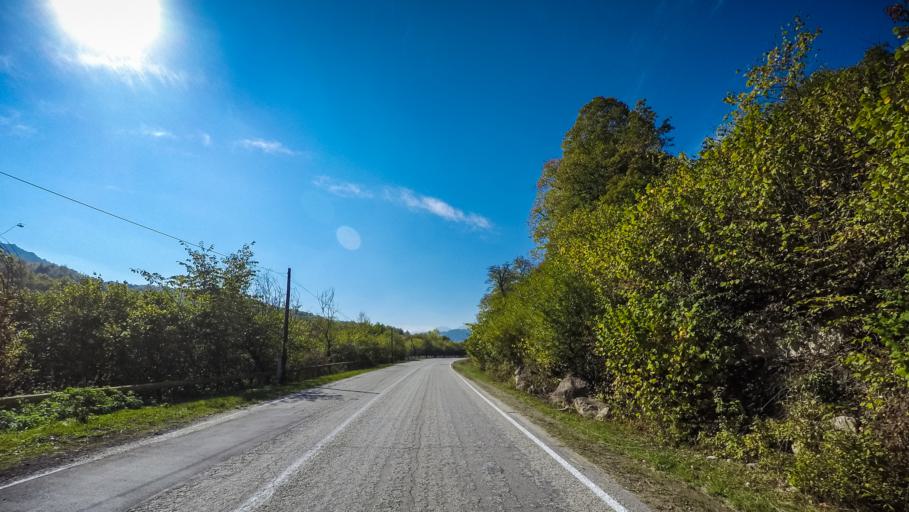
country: RU
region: Kabardino-Balkariya
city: Zayukovo
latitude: 43.5166
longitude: 43.3191
